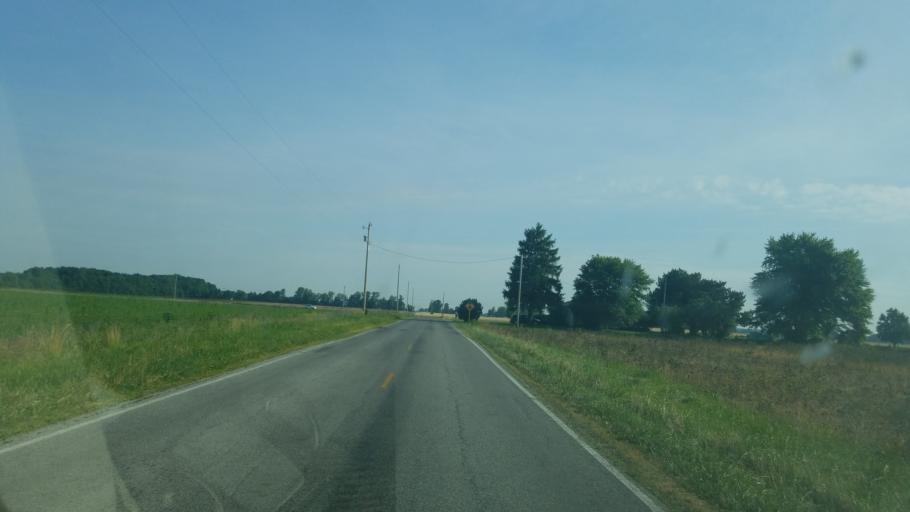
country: US
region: Ohio
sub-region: Hancock County
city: Arlington
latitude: 40.9044
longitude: -83.6985
